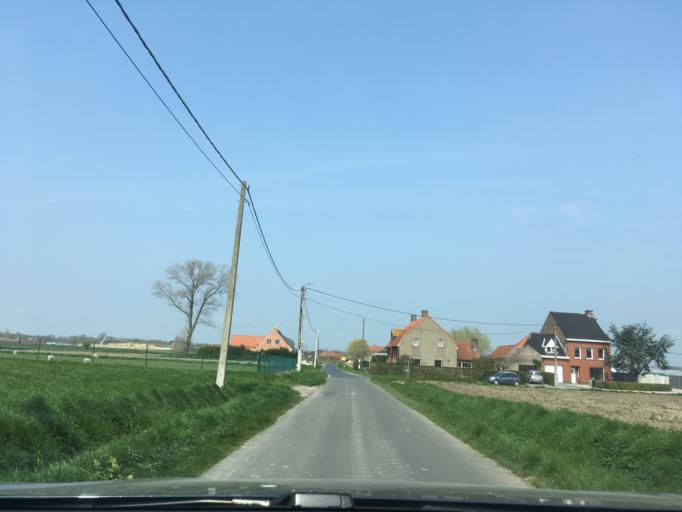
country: BE
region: Flanders
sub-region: Provincie West-Vlaanderen
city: Ardooie
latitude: 50.9916
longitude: 3.1898
